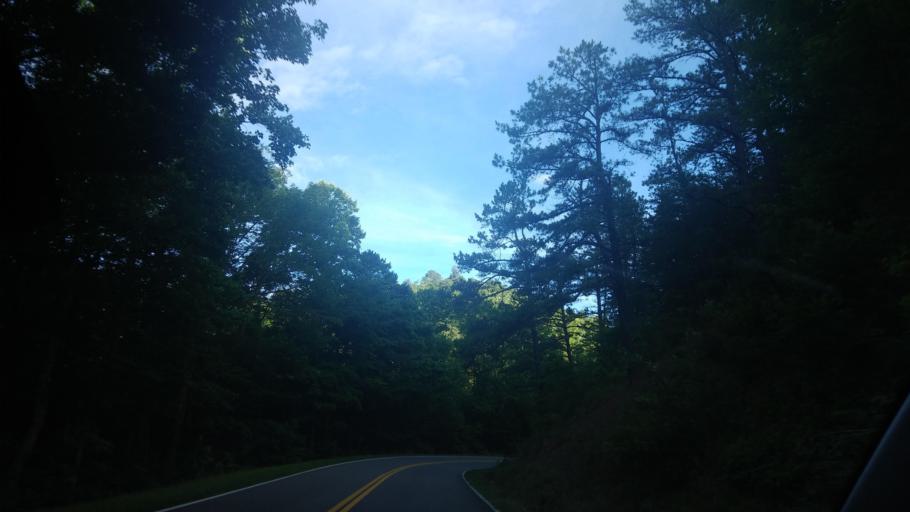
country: US
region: Tennessee
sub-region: Cocke County
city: Newport
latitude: 35.8198
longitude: -83.2128
